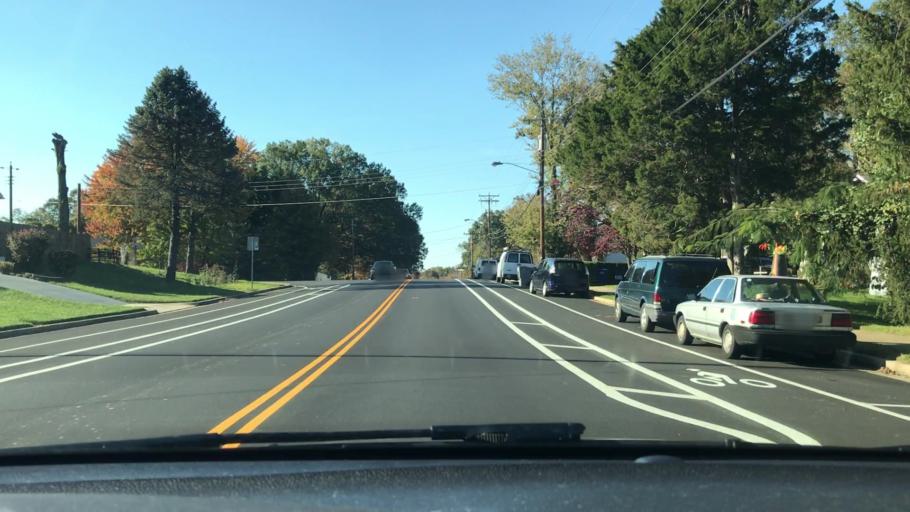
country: US
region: Virginia
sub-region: Fairfax County
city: Annandale
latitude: 38.8375
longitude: -77.1922
